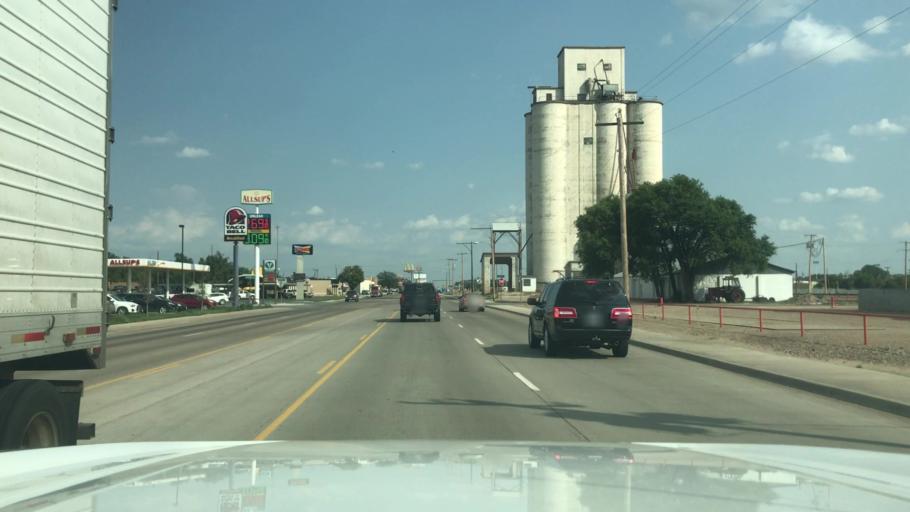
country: US
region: Texas
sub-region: Dallam County
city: Dalhart
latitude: 36.0629
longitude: -102.5180
